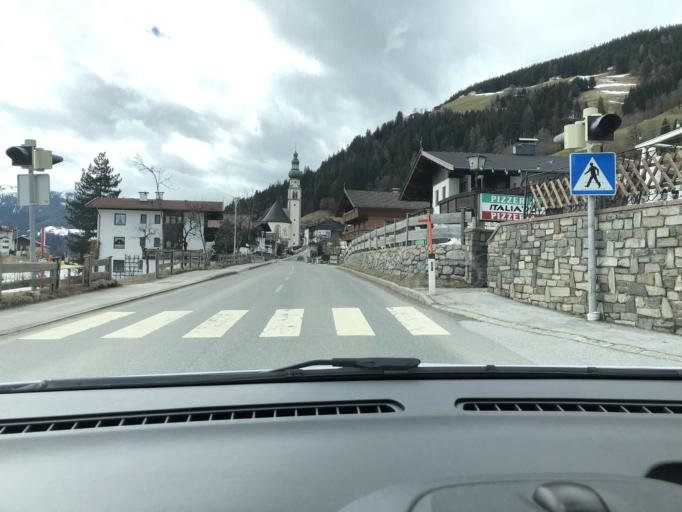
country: AT
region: Tyrol
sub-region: Politischer Bezirk Kufstein
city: Worgl
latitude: 47.4453
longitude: 12.0531
